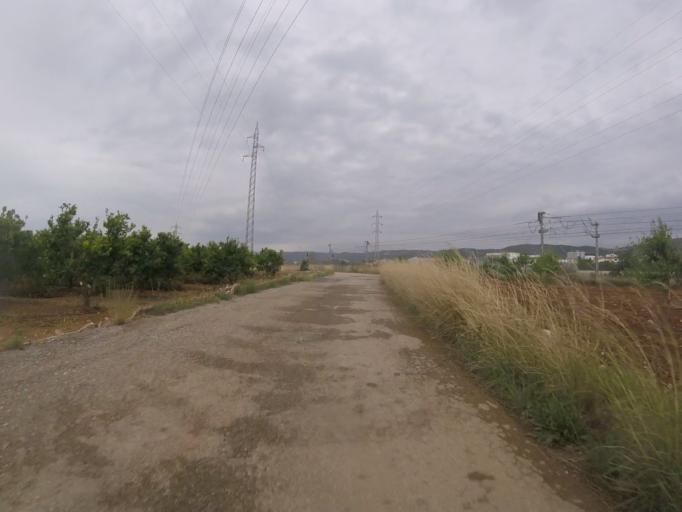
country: ES
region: Valencia
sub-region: Provincia de Castello
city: Torreblanca
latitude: 40.2191
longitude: 0.2069
